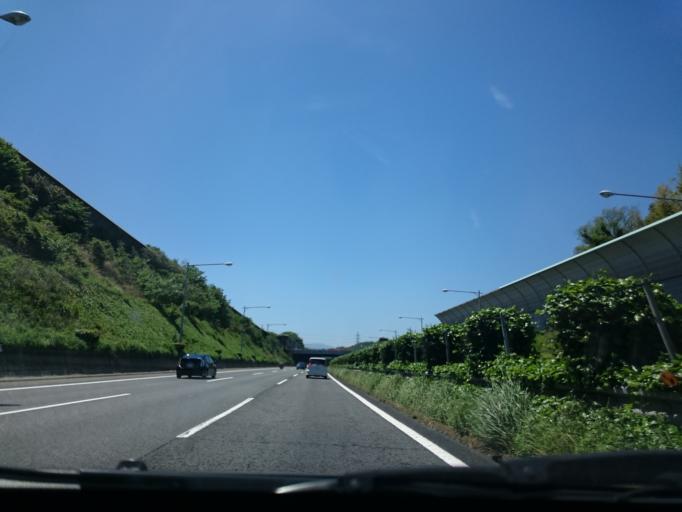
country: JP
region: Kanagawa
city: Isehara
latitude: 35.4169
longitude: 139.3263
